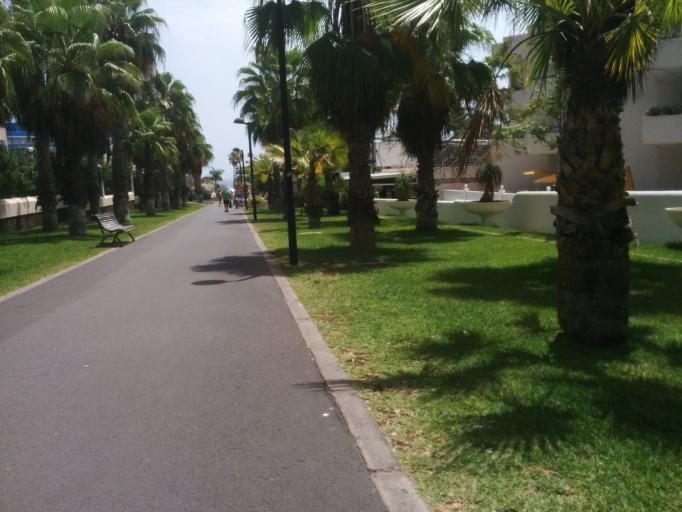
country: ES
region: Canary Islands
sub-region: Provincia de Santa Cruz de Tenerife
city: Playa de las Americas
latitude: 28.0562
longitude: -16.7300
